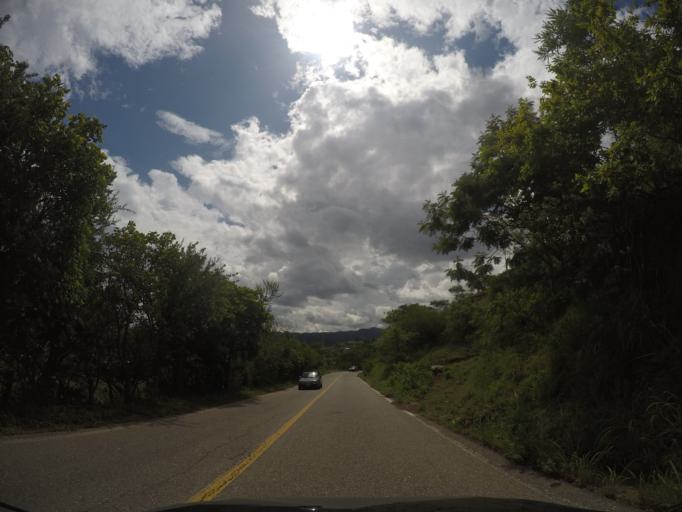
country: MX
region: Oaxaca
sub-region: San Jeronimo Coatlan
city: San Cristobal Honduras
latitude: 16.4331
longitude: -97.0604
